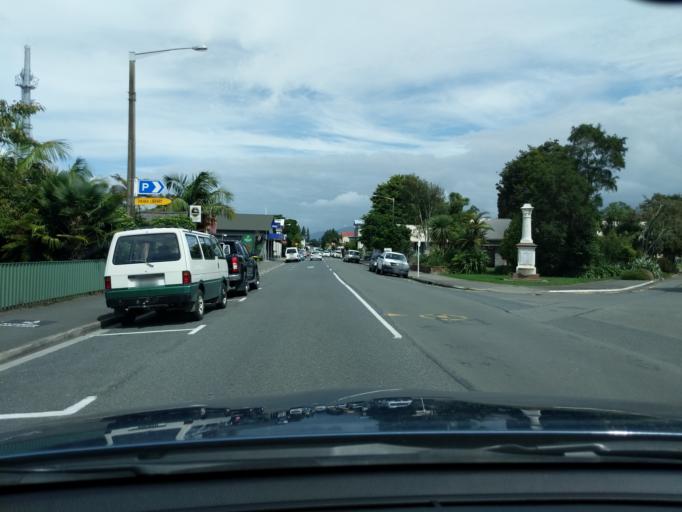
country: NZ
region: Tasman
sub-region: Tasman District
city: Takaka
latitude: -40.8571
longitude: 172.8065
